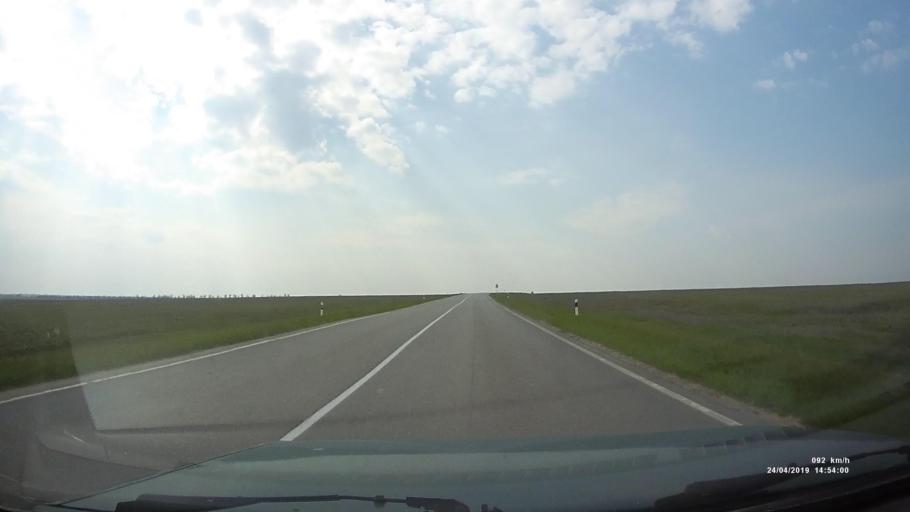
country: RU
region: Rostov
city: Remontnoye
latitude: 46.5324
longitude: 43.6461
